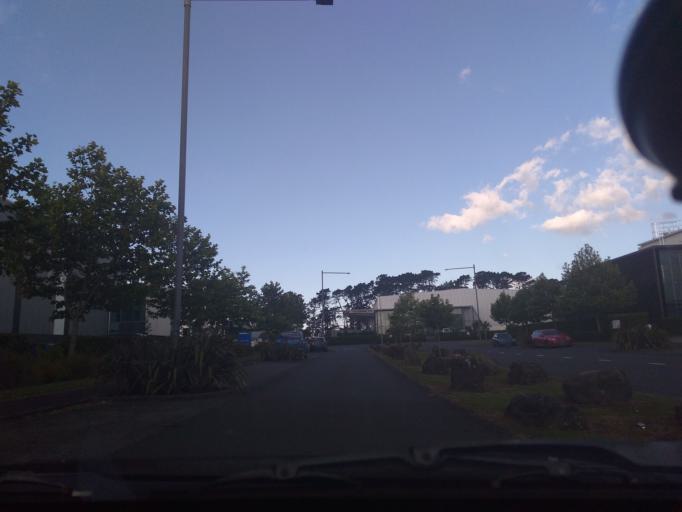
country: NZ
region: Auckland
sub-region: Auckland
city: Tamaki
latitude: -36.9324
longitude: 174.8746
